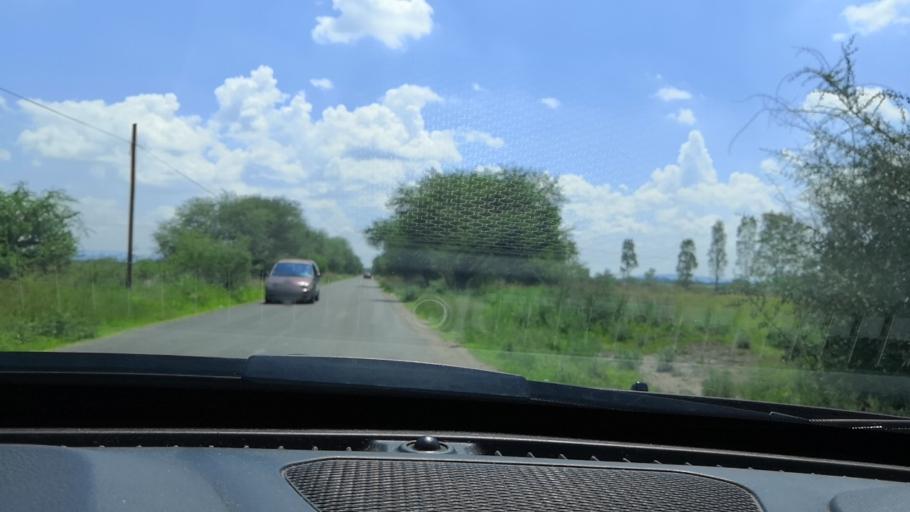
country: MX
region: Guanajuato
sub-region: Leon
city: Plan Guanajuato (La Sandia)
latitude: 20.9417
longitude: -101.6259
